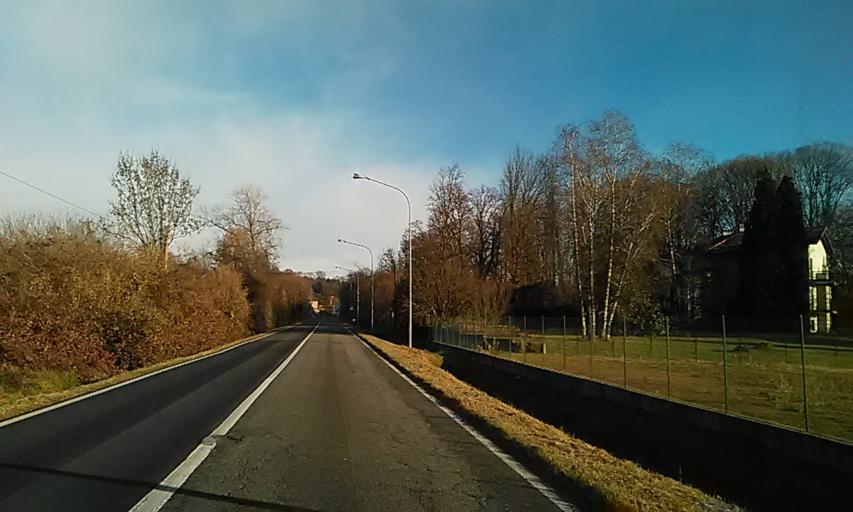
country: IT
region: Piedmont
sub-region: Provincia di Vercelli
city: Roasio
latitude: 45.5896
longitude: 8.2722
